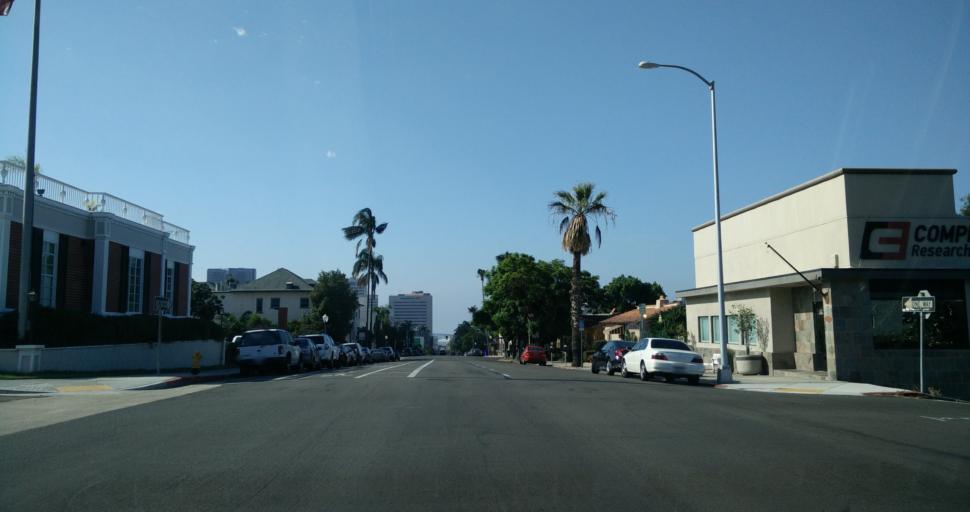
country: US
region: California
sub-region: San Diego County
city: San Diego
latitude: 32.7283
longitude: -117.1612
